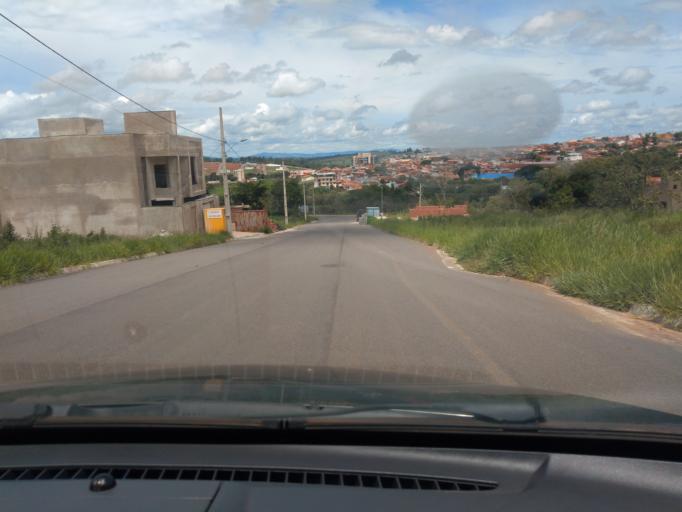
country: BR
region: Minas Gerais
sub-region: Tres Coracoes
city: Tres Coracoes
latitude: -21.6786
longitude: -45.2758
